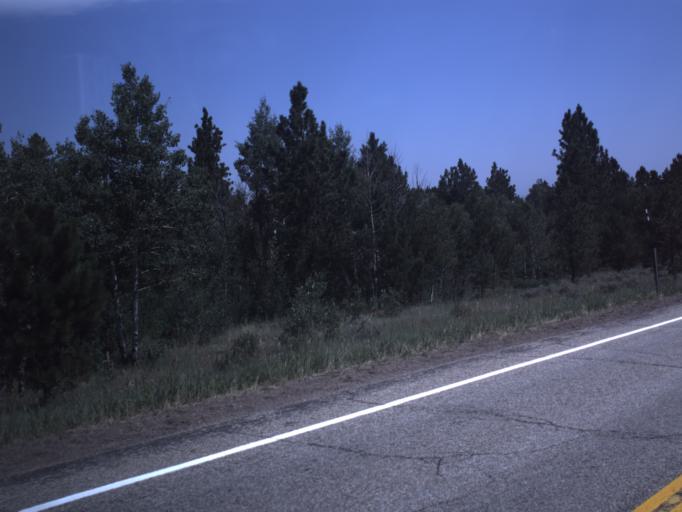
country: US
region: Utah
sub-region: Daggett County
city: Manila
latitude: 40.8480
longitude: -109.6404
